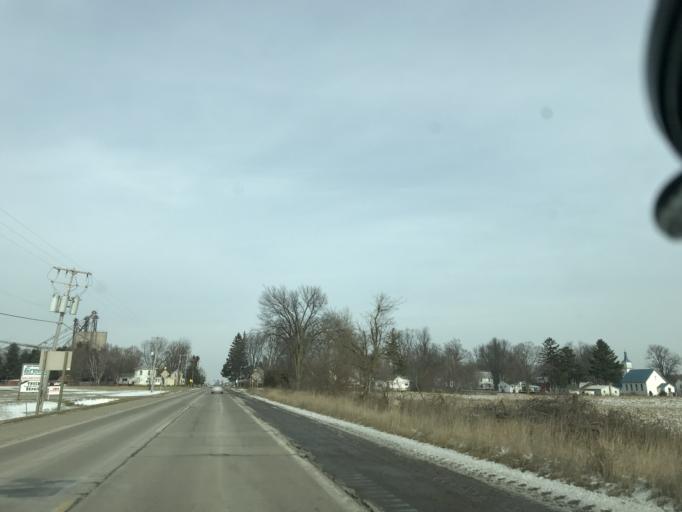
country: US
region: Michigan
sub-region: Ionia County
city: Lake Odessa
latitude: 42.7582
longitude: -85.0744
